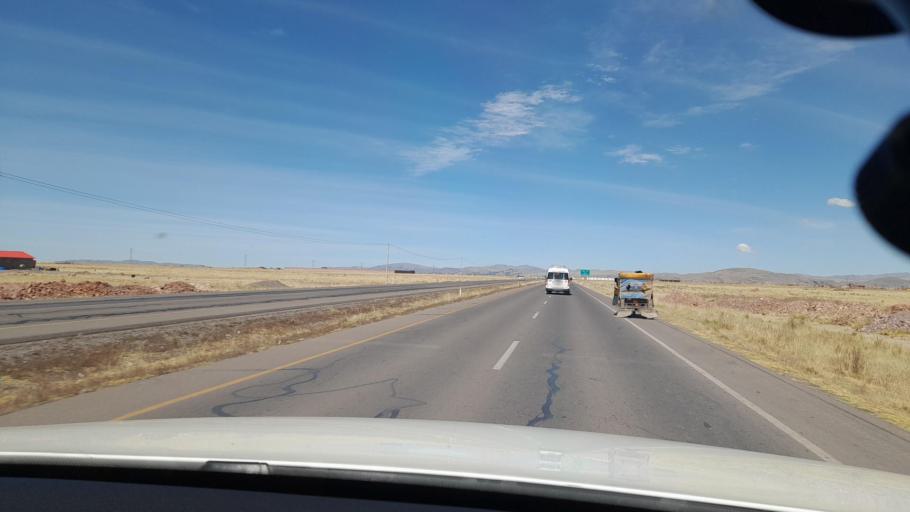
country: PE
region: Puno
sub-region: San Roman
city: Caracoto
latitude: -15.5962
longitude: -70.0961
